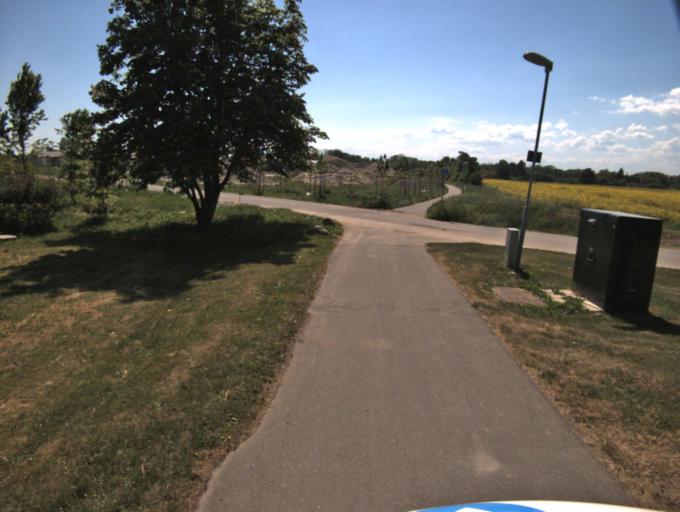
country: SE
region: Skane
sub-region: Kristianstads Kommun
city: Kristianstad
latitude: 56.0159
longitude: 14.2214
